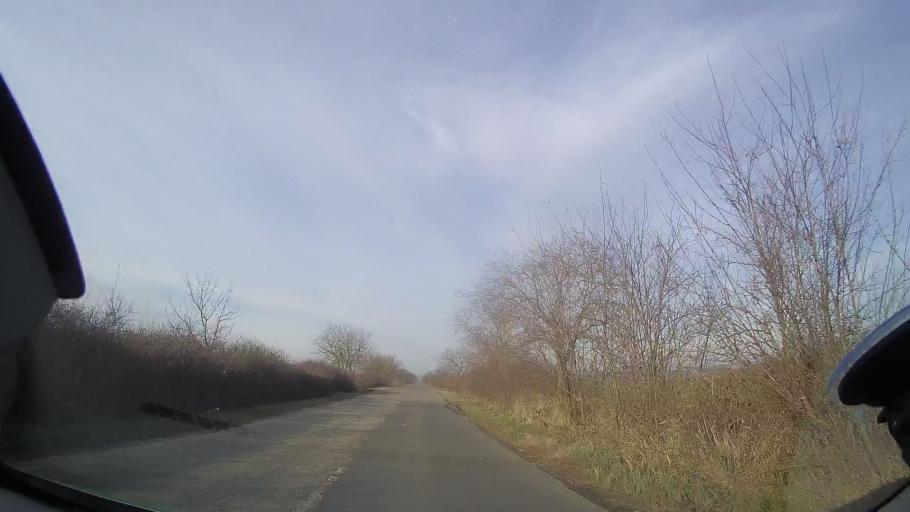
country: RO
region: Bihor
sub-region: Comuna Spinus
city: Spinus
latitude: 47.2157
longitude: 22.1756
